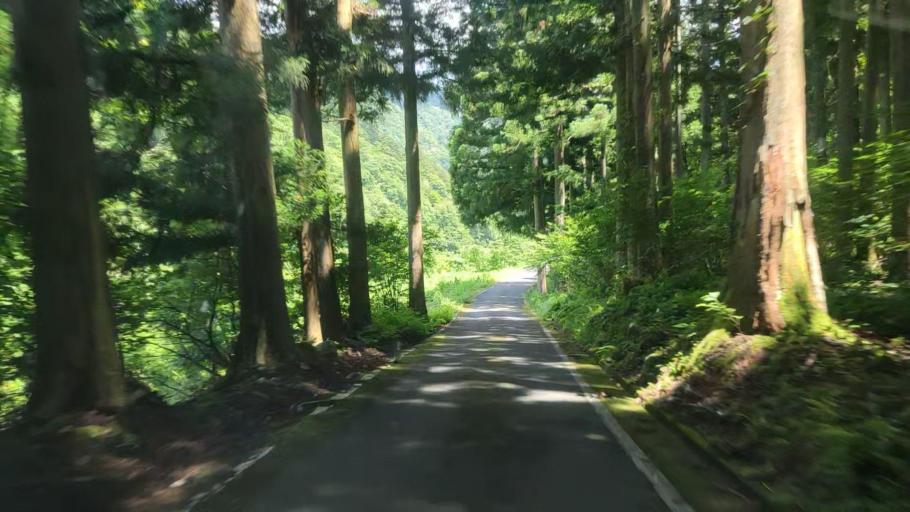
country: JP
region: Fukui
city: Ono
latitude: 35.7563
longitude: 136.5722
